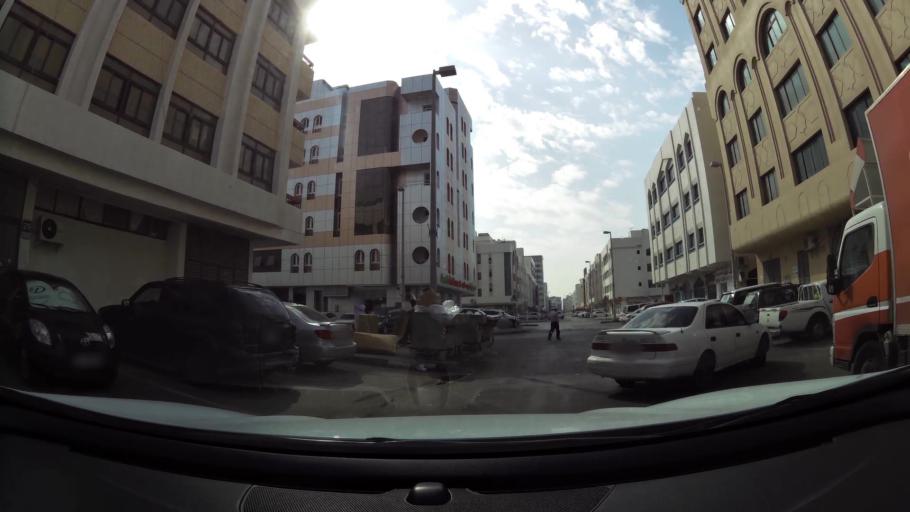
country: AE
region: Abu Dhabi
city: Abu Dhabi
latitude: 24.3242
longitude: 54.5376
